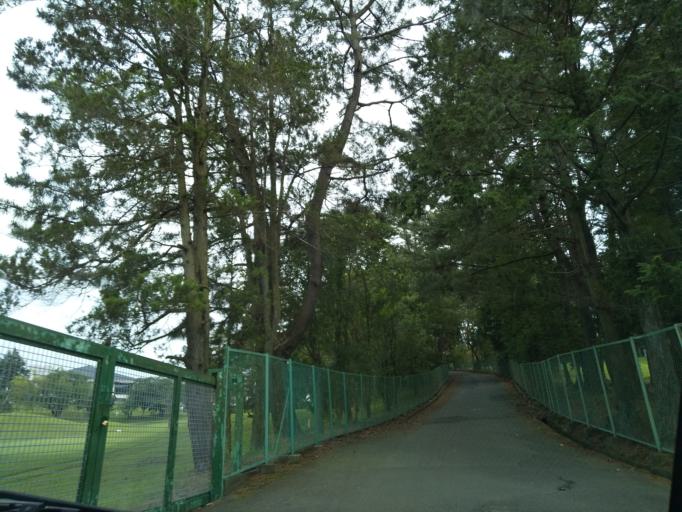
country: JP
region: Kanagawa
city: Atsugi
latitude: 35.4756
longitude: 139.3240
